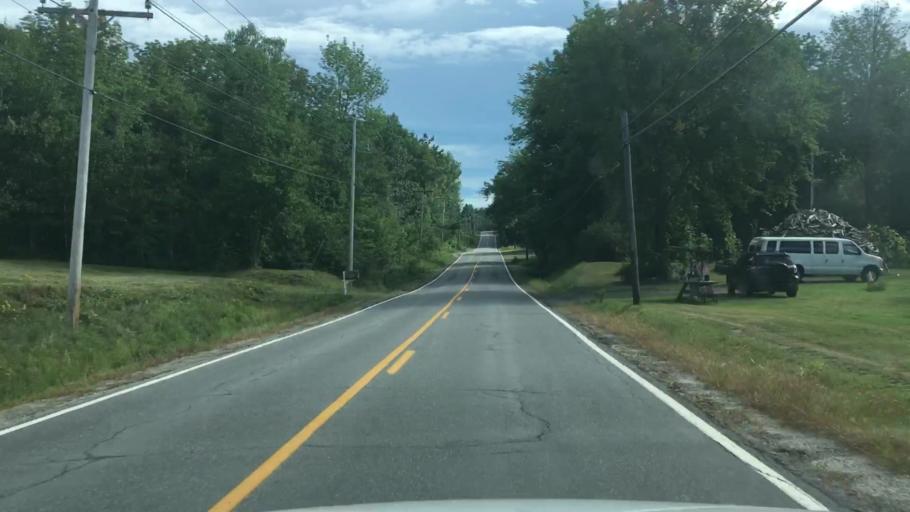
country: US
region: Maine
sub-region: Hancock County
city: Ellsworth
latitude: 44.4934
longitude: -68.4202
